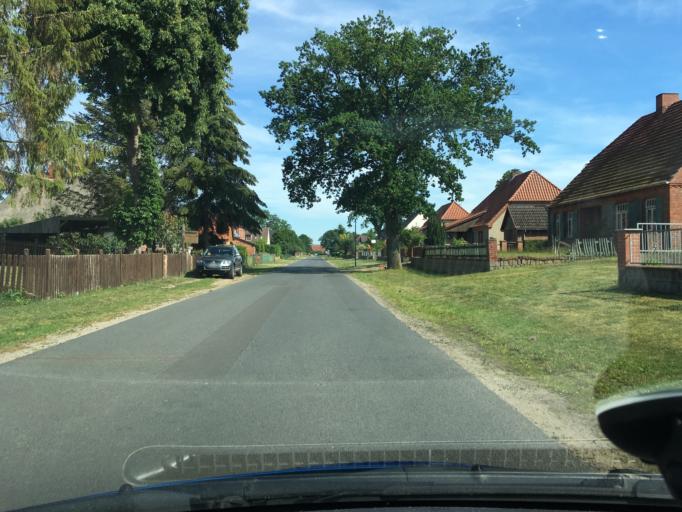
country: DE
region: Lower Saxony
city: Neu Darchau
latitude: 53.3448
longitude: 10.8521
